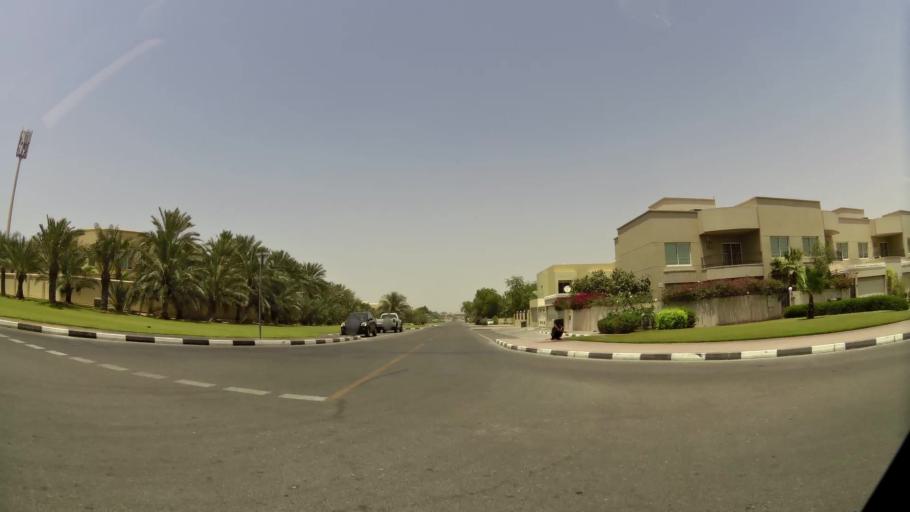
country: AE
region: Dubai
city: Dubai
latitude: 25.1665
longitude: 55.2212
